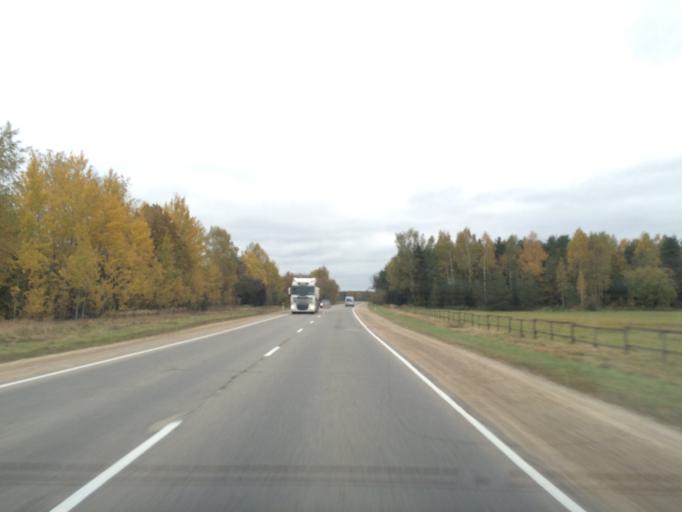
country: LV
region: Koknese
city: Koknese
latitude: 56.6109
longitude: 25.5014
